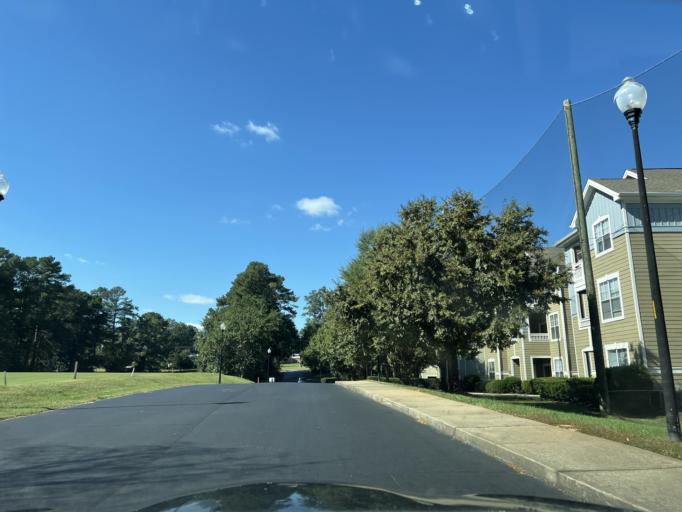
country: US
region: North Carolina
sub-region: Wake County
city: Raleigh
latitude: 35.7415
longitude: -78.6632
